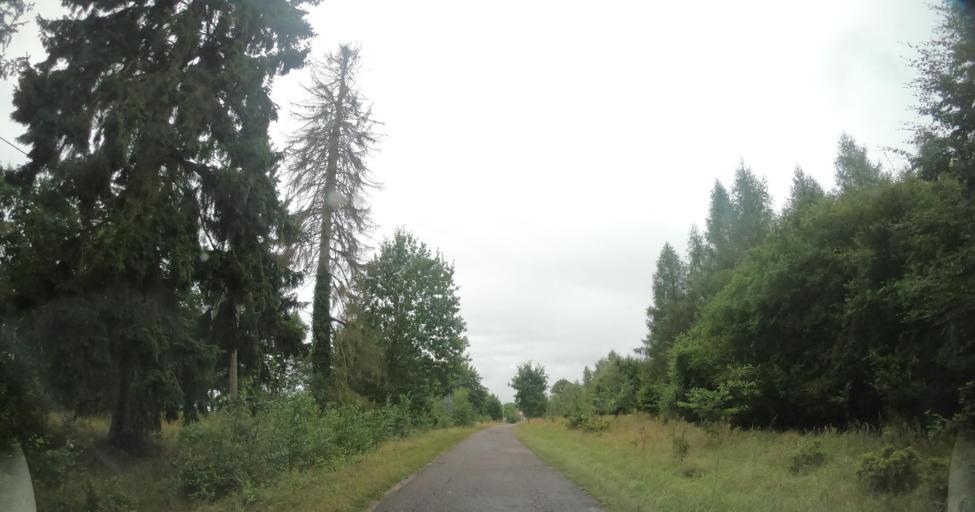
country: PL
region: West Pomeranian Voivodeship
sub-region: Powiat lobeski
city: Wegorzyno
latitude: 53.5277
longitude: 15.4981
